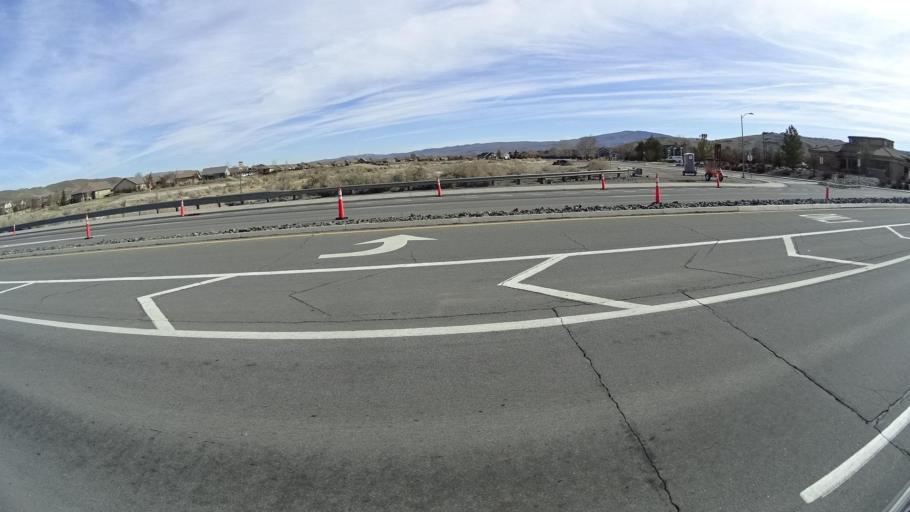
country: US
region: Nevada
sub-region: Washoe County
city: Sun Valley
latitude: 39.5897
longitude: -119.7288
